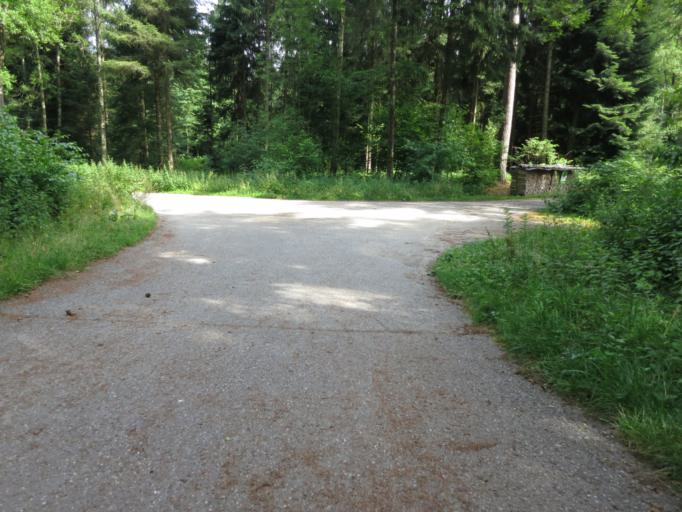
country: CH
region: Zurich
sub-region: Bezirk Hinwil
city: Bubikon
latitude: 47.2566
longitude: 8.8291
